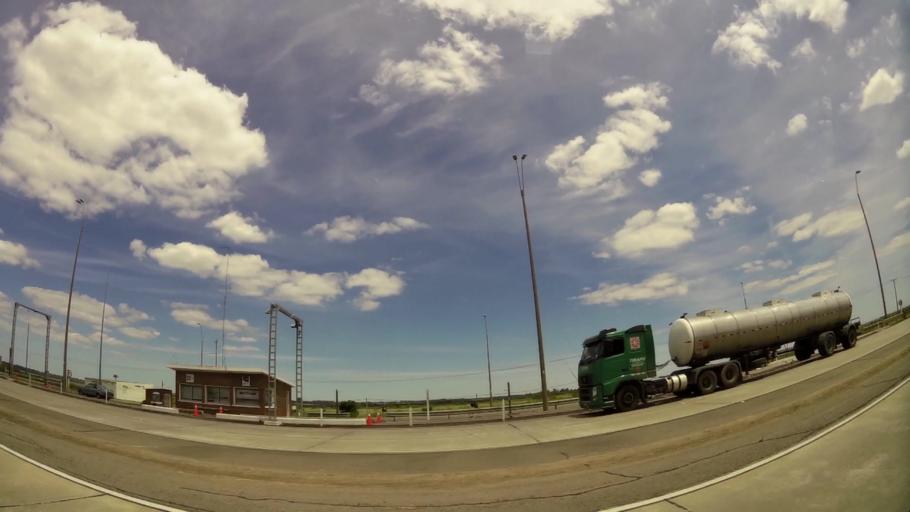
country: UY
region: San Jose
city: Delta del Tigre
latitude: -34.7751
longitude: -56.3775
